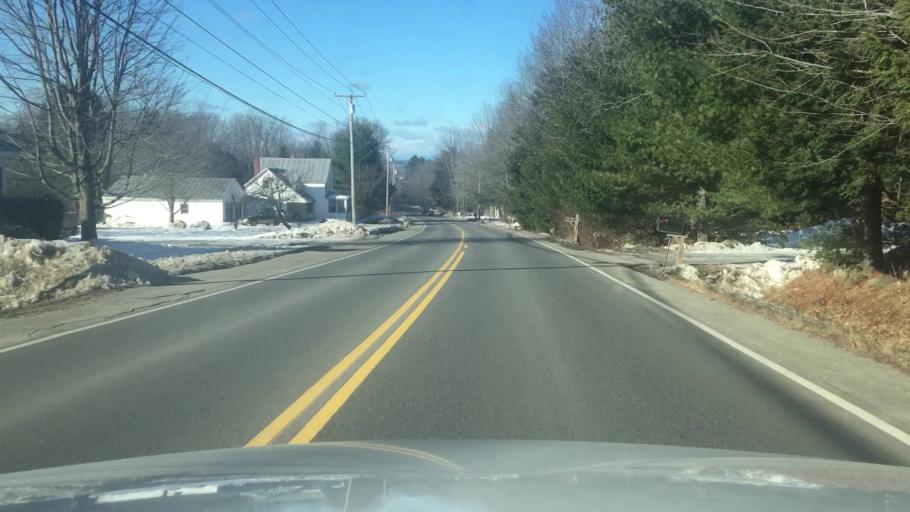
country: US
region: Maine
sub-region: Somerset County
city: Skowhegan
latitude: 44.7463
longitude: -69.6955
